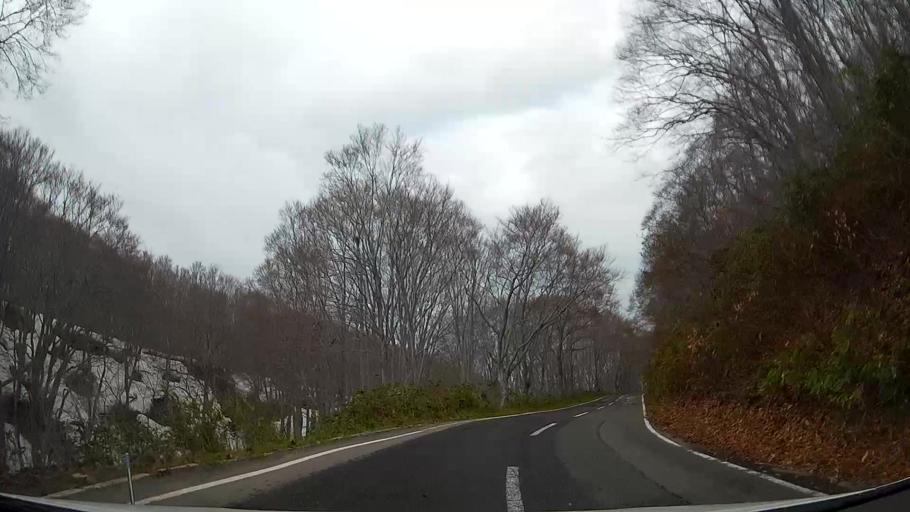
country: JP
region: Aomori
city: Aomori Shi
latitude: 40.6496
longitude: 140.8476
